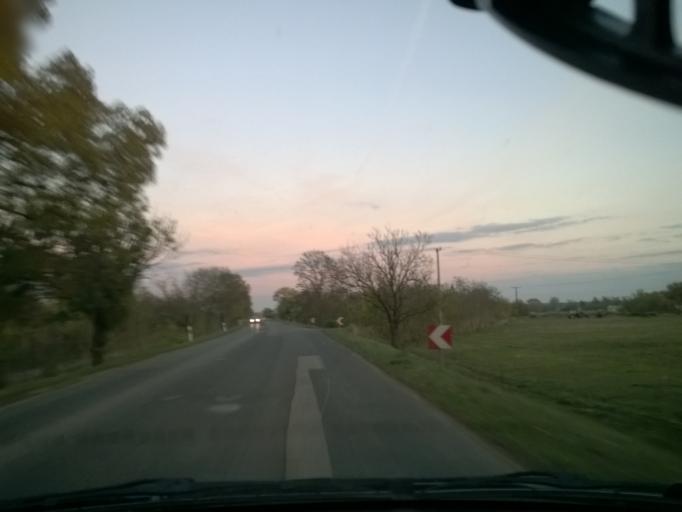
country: HU
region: Csongrad
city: Csongrad
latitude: 46.6878
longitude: 20.1693
